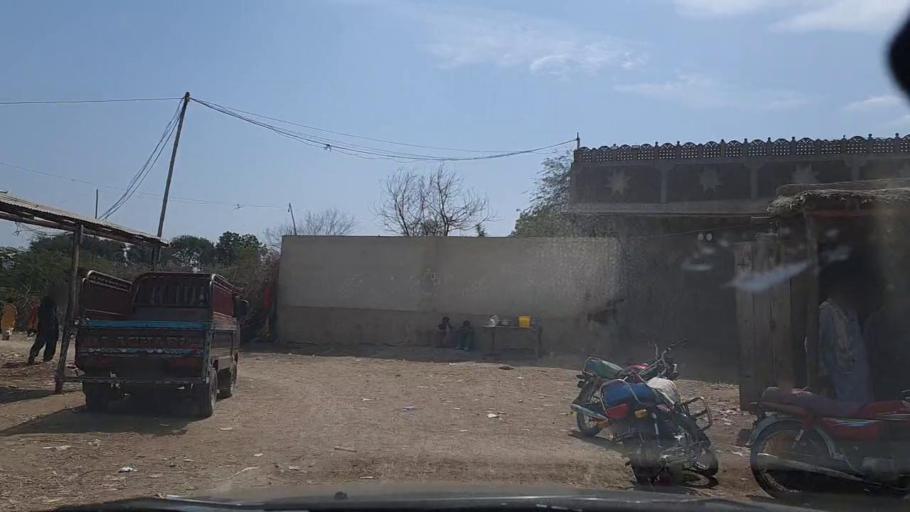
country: PK
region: Sindh
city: Mirpur Batoro
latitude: 24.6404
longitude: 68.1614
